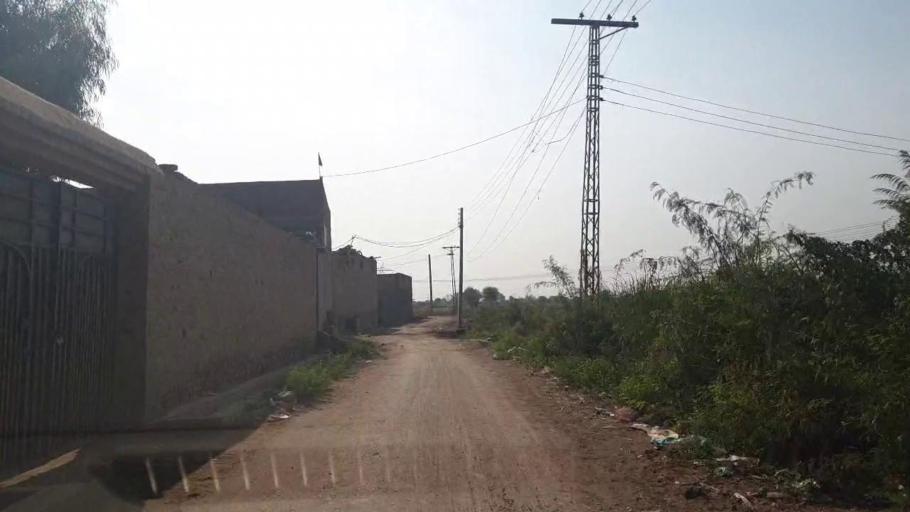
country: PK
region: Sindh
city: Hyderabad
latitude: 25.4699
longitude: 68.3790
